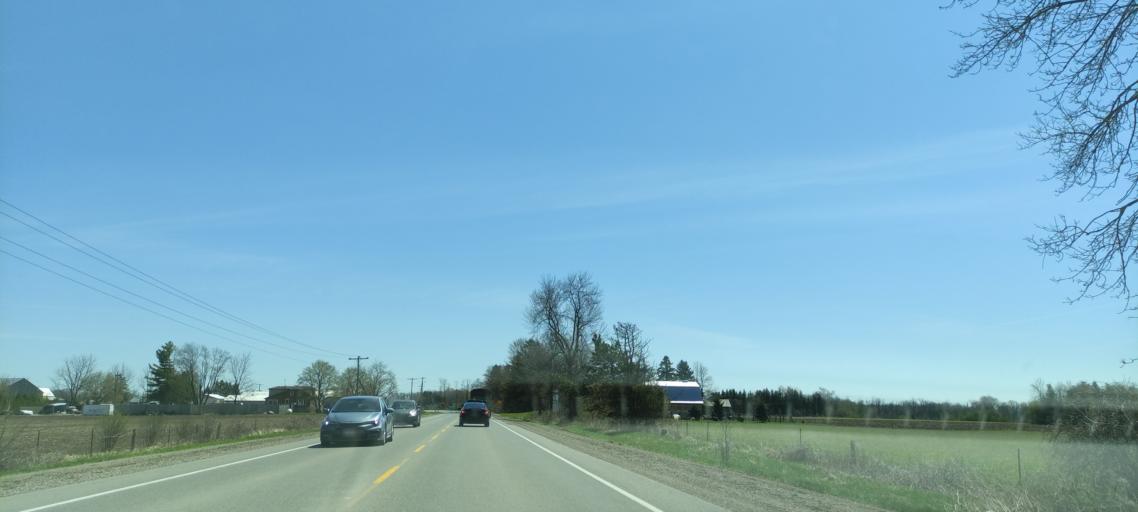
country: CA
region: Ontario
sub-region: Wellington County
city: Guelph
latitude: 43.5746
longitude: -80.4039
